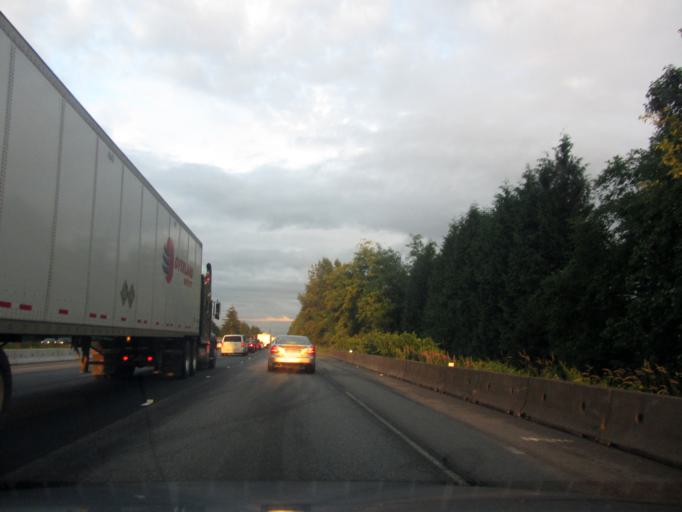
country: CA
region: British Columbia
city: Langley
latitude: 49.1127
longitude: -122.5218
